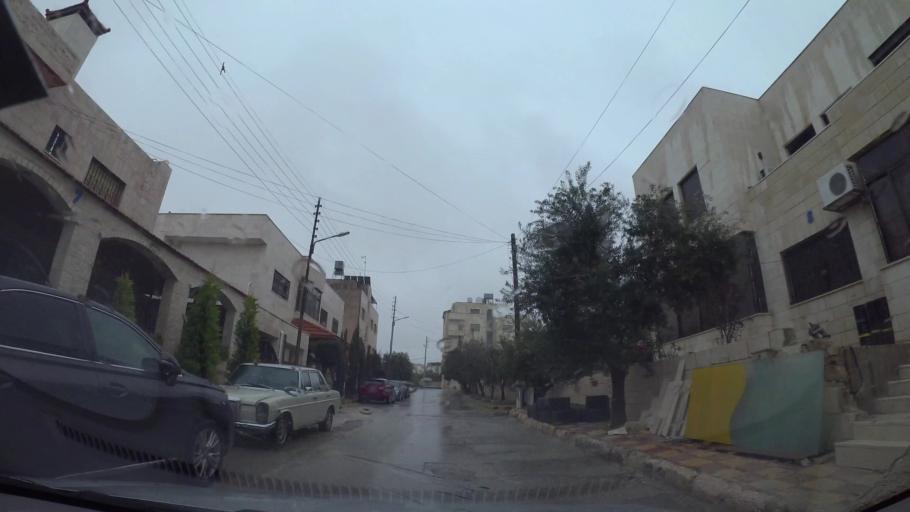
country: JO
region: Amman
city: Al Jubayhah
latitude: 32.0301
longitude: 35.8918
